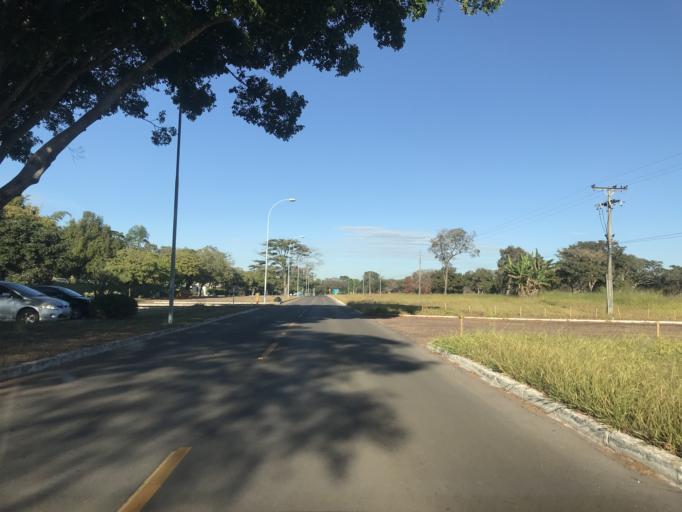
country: BR
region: Federal District
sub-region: Brasilia
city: Brasilia
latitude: -15.8293
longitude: -47.8969
